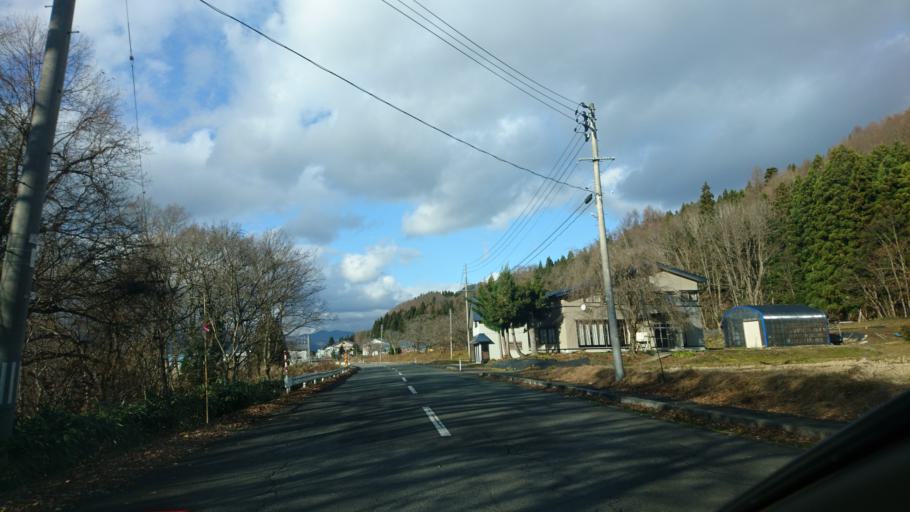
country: JP
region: Akita
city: Yokotemachi
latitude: 39.3714
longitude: 140.7701
